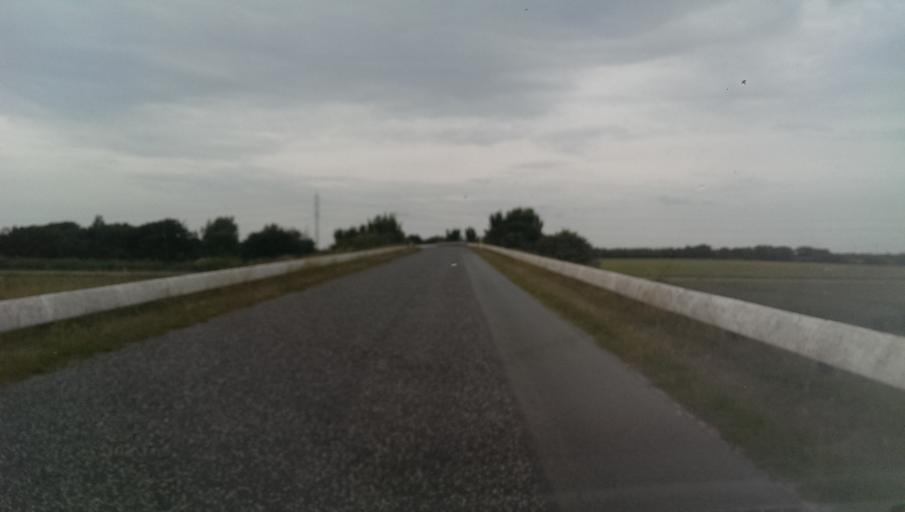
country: DK
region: South Denmark
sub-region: Esbjerg Kommune
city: Bramming
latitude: 55.4358
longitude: 8.6501
